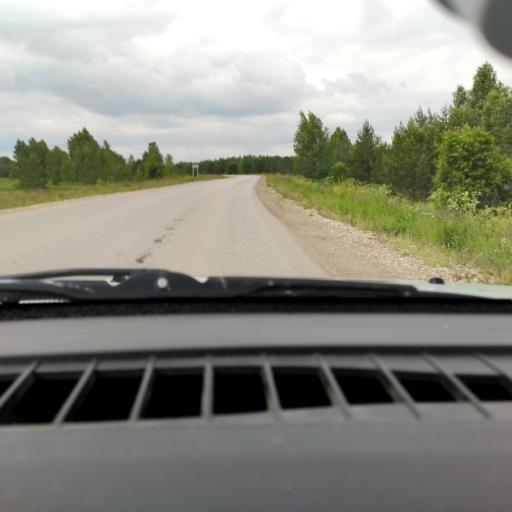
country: RU
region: Perm
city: Orda
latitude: 57.1427
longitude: 56.7358
